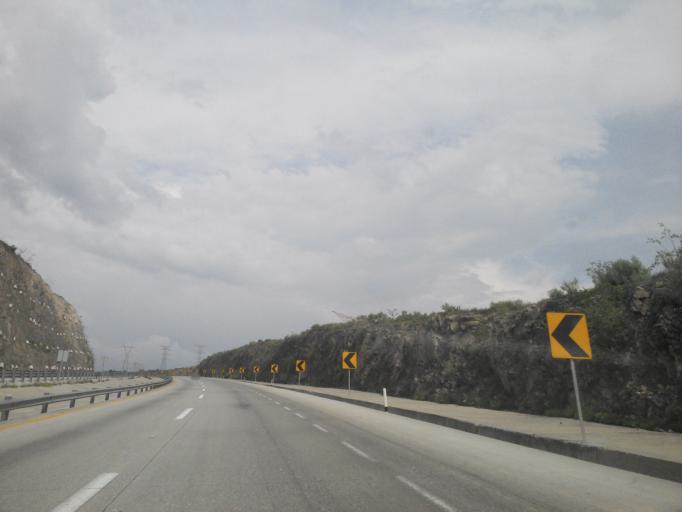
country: MX
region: Mexico
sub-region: Apaxco
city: Colonia Juarez
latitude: 20.0218
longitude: -99.1677
